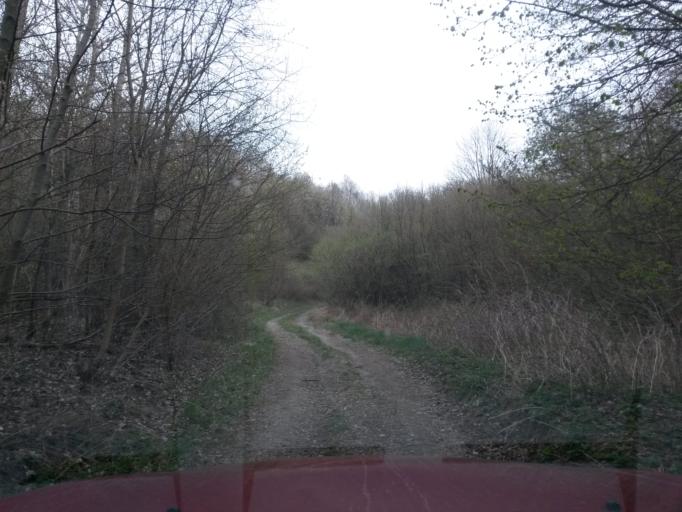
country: SK
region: Kosicky
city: Kosice
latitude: 48.7431
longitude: 21.1185
